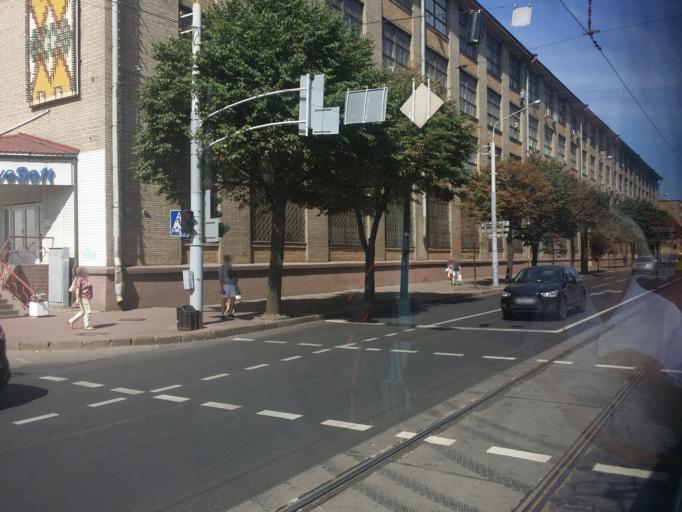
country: BY
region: Minsk
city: Minsk
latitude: 53.9173
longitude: 27.5842
